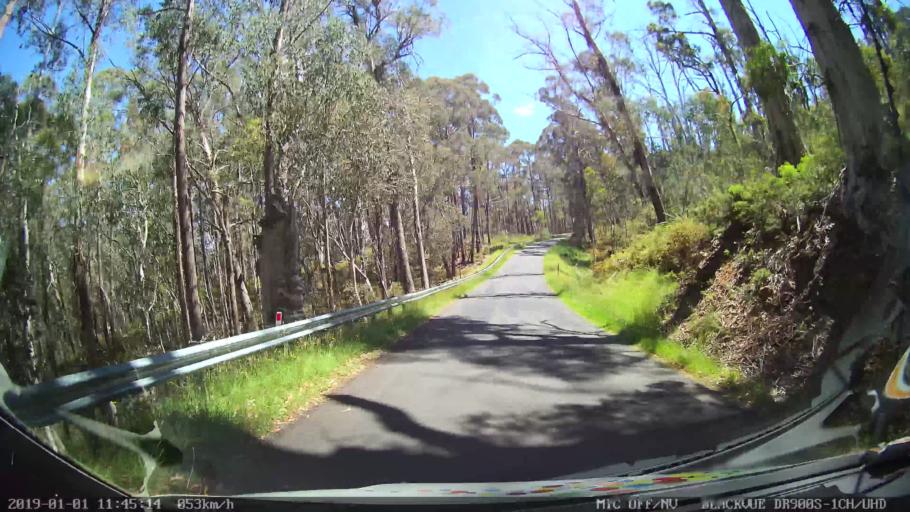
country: AU
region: New South Wales
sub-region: Snowy River
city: Jindabyne
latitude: -35.8984
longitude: 148.3954
